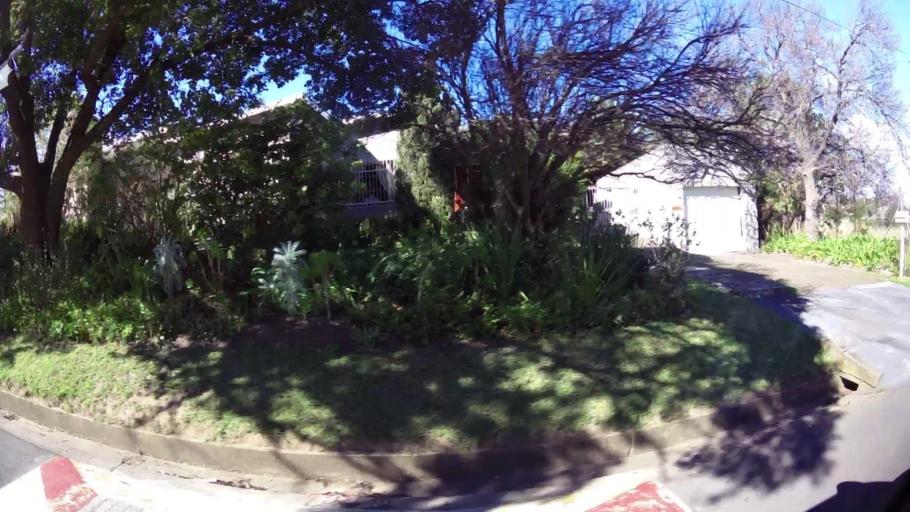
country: ZA
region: Western Cape
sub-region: Overberg District Municipality
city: Swellendam
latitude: -34.0259
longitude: 20.4451
